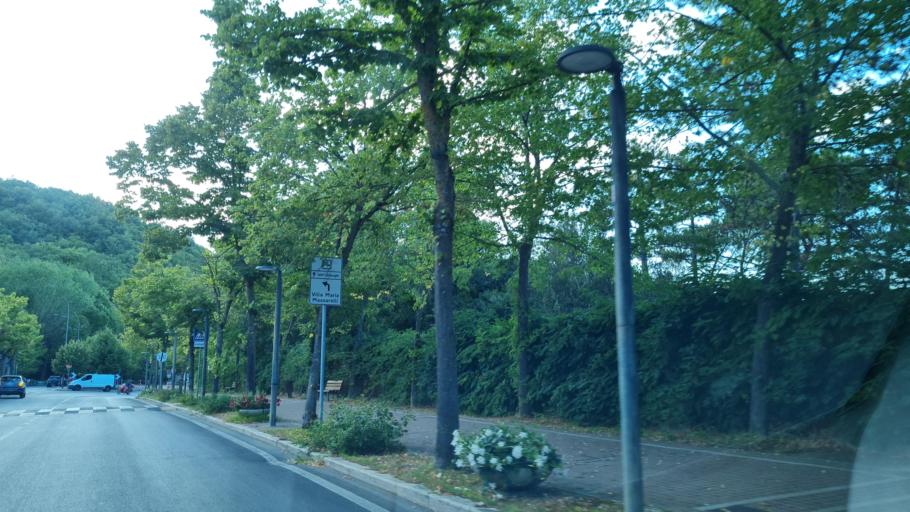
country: IT
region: Tuscany
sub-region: Provincia di Siena
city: Chianciano Terme
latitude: 43.0390
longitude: 11.8194
